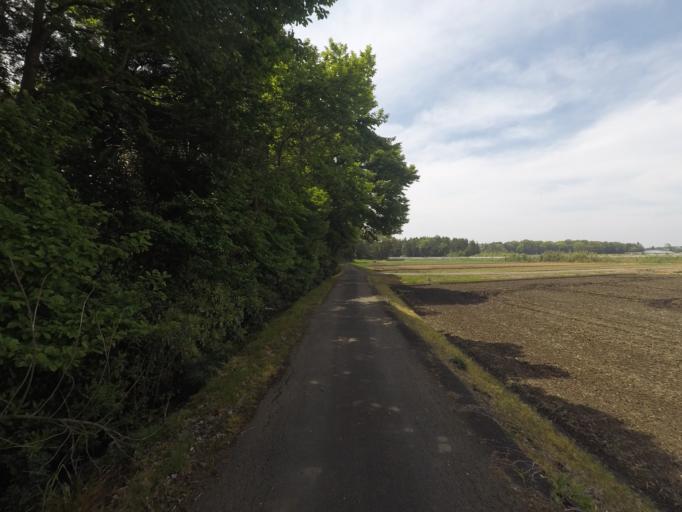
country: JP
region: Ibaraki
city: Ishige
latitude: 36.0888
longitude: 140.0295
